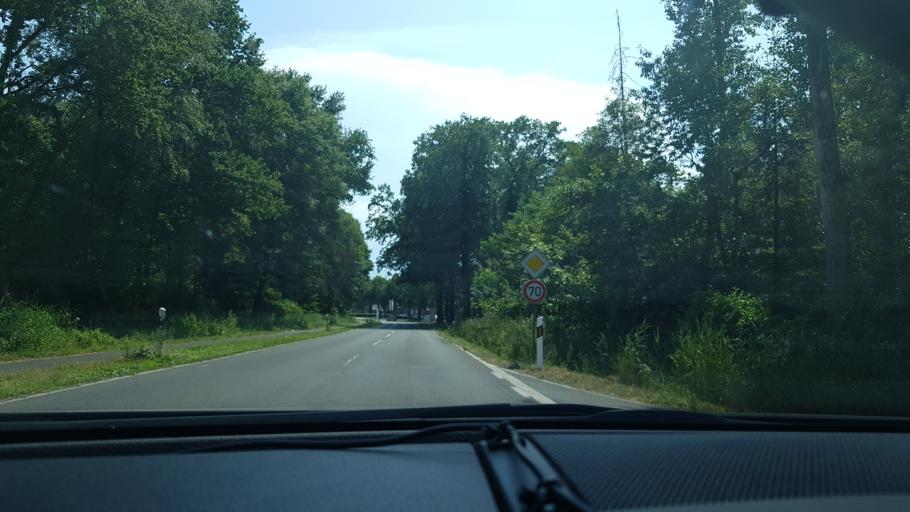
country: DE
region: North Rhine-Westphalia
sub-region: Regierungsbezirk Dusseldorf
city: Bruggen
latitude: 51.2332
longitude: 6.1869
